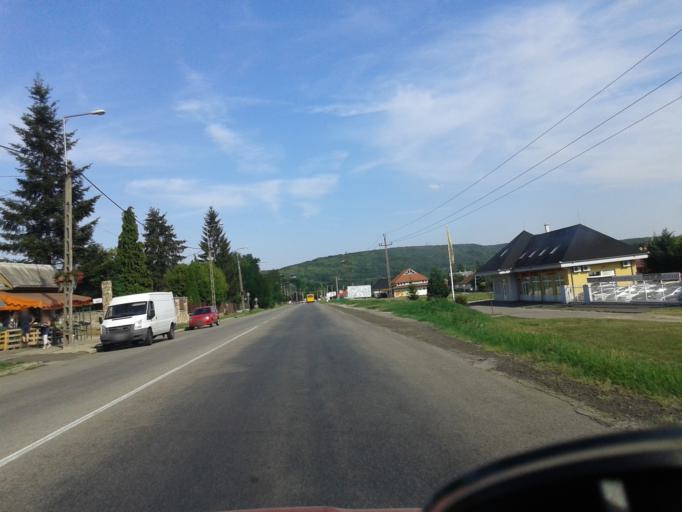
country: HU
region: Pest
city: Godollo
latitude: 47.5996
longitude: 19.3868
